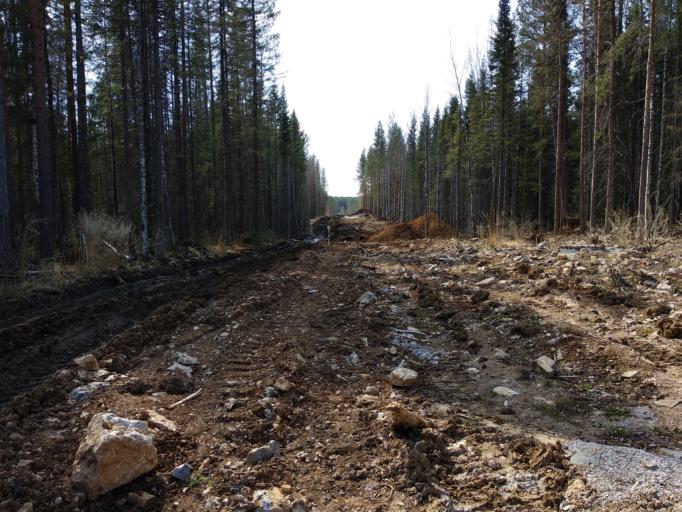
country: RU
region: Sverdlovsk
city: Krasnotur'insk
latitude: 59.6649
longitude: 60.1722
